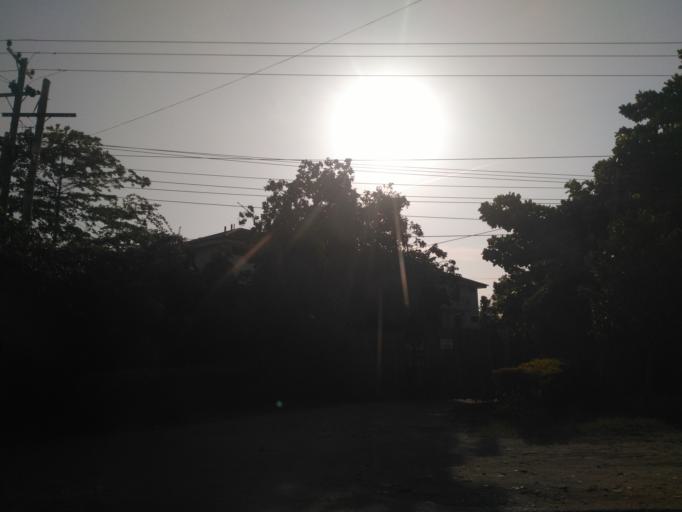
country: TZ
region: Dar es Salaam
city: Magomeni
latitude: -6.7563
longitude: 39.2760
